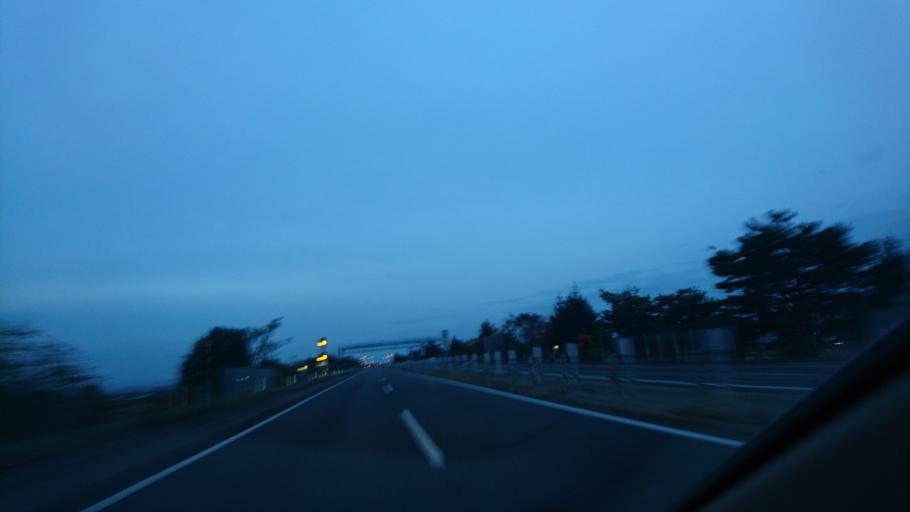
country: JP
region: Iwate
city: Morioka-shi
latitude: 39.6273
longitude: 141.1285
